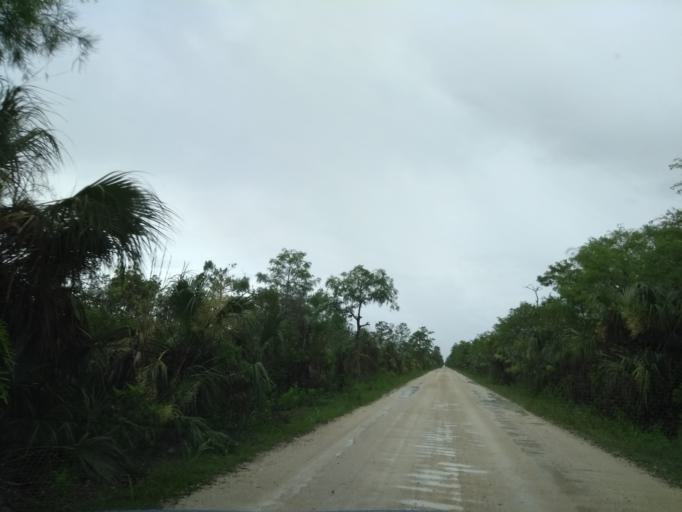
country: US
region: Florida
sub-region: Miami-Dade County
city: The Hammocks
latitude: 25.7602
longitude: -81.0212
